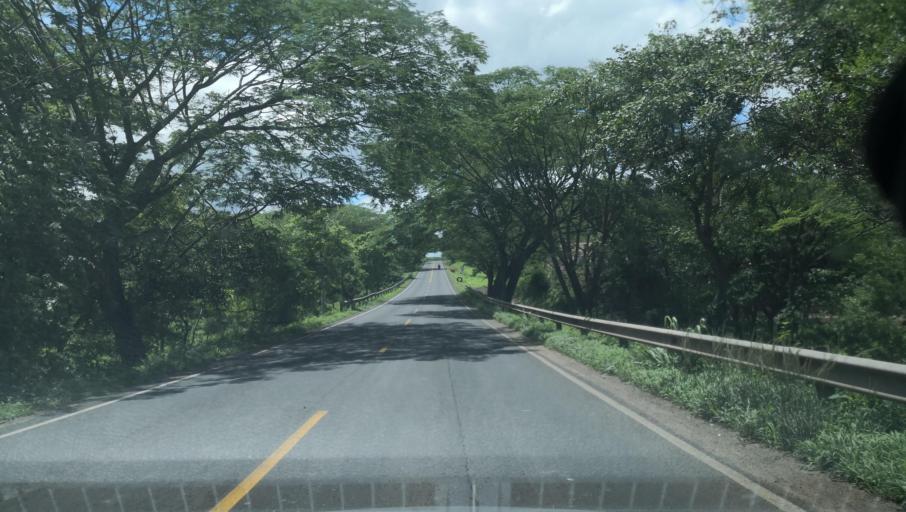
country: NI
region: Esteli
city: Condega
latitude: 13.3840
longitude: -86.4014
